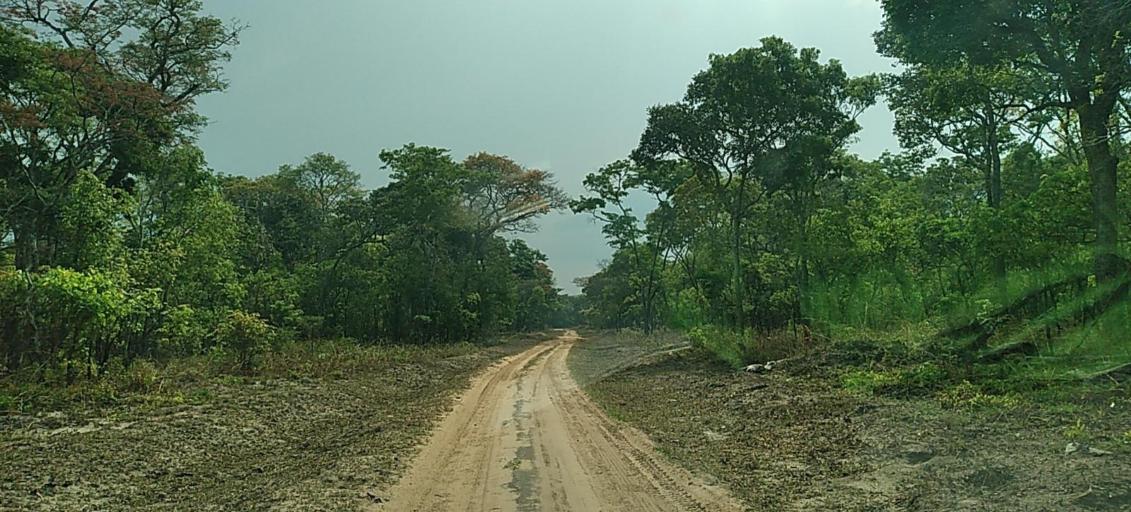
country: ZM
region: North-Western
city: Mwinilunga
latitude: -11.4701
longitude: 24.4875
